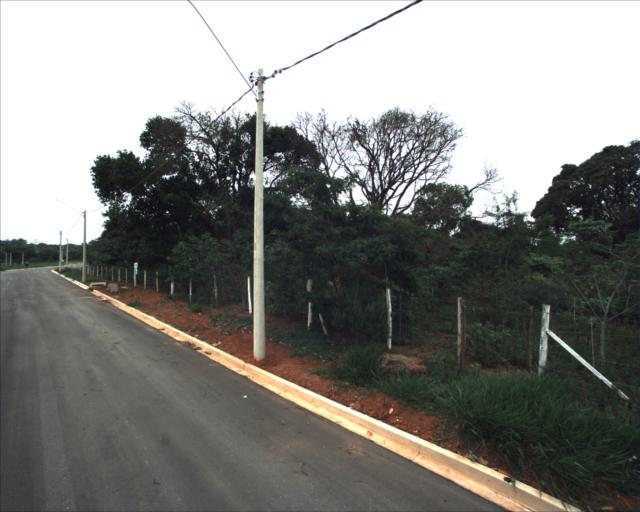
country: BR
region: Sao Paulo
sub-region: Sorocaba
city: Sorocaba
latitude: -23.4188
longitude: -47.4277
